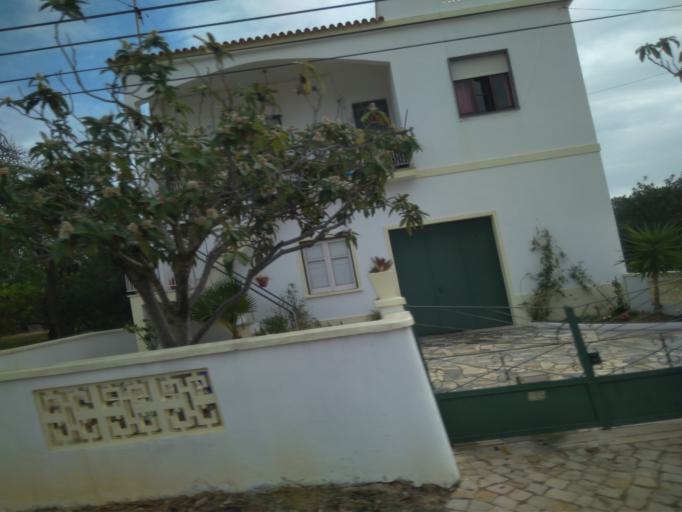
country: PT
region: Faro
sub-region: Faro
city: Santa Barbara de Nexe
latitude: 37.0846
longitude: -7.9587
